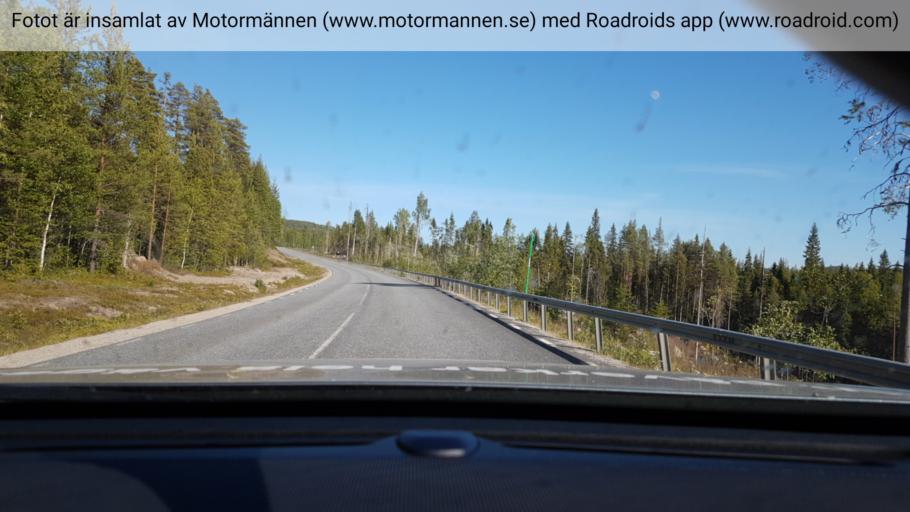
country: SE
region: Vaesterbotten
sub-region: Lycksele Kommun
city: Lycksele
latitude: 64.4545
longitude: 18.9175
